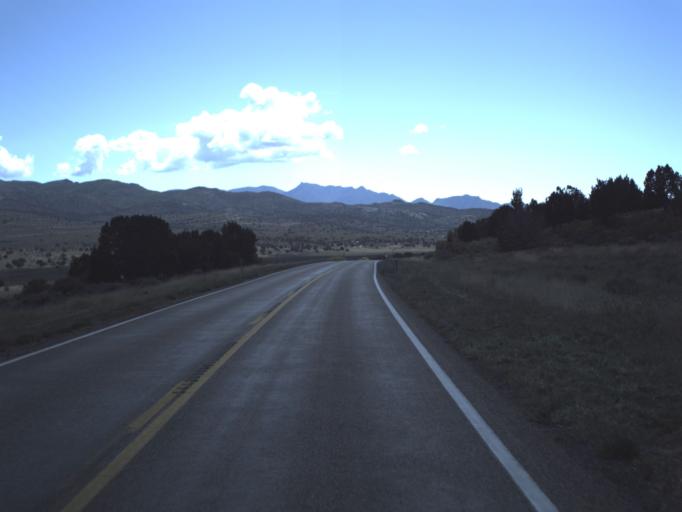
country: US
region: Utah
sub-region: Washington County
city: Enterprise
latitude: 37.5163
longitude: -113.6354
